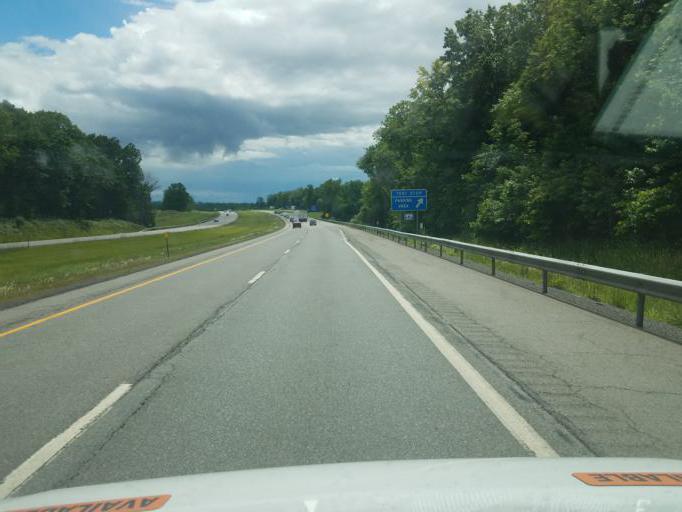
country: US
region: New York
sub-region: Monroe County
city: Pittsford
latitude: 43.0171
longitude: -77.4864
